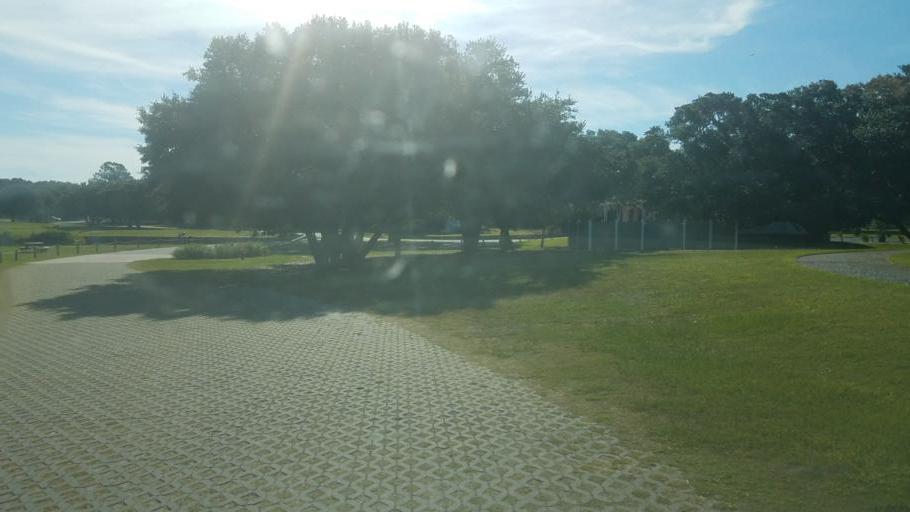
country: US
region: North Carolina
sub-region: Currituck County
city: Currituck
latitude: 36.3736
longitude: -75.8322
